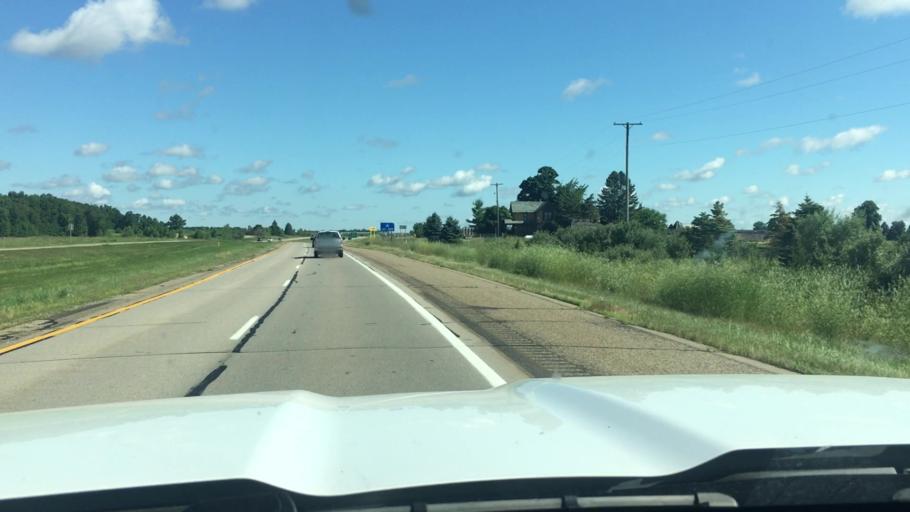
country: US
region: Michigan
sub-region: Gratiot County
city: Ithaca
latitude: 43.1633
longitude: -84.5630
